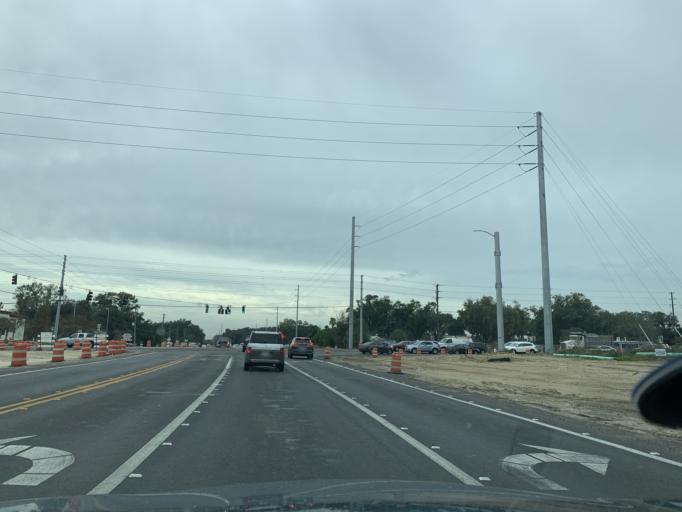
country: US
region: Florida
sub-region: Pasco County
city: Zephyrhills West
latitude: 28.2195
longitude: -82.2464
